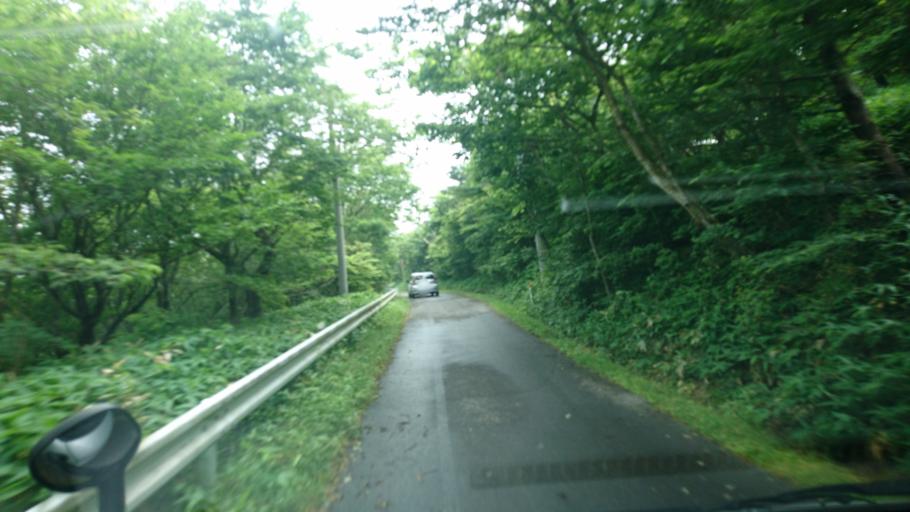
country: JP
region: Iwate
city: Ofunato
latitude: 39.1350
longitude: 141.7548
